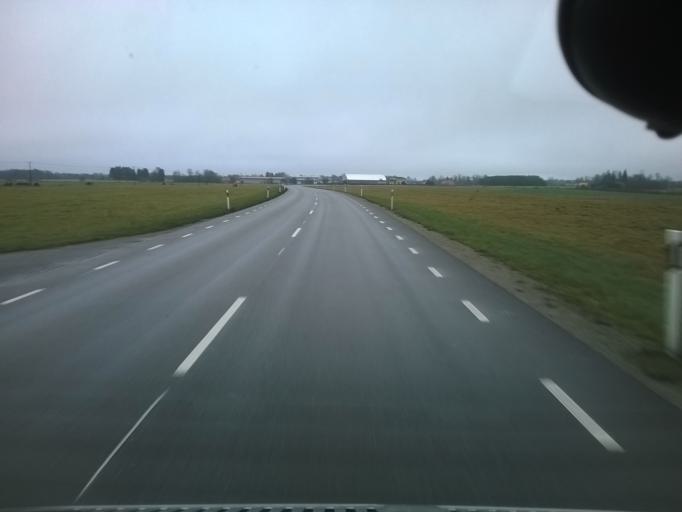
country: EE
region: Harju
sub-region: Saku vald
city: Saku
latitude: 59.2633
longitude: 24.7196
